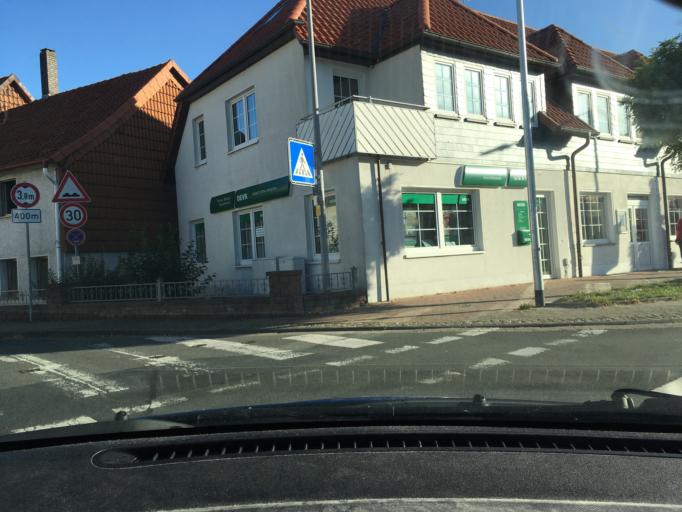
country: DE
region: Lower Saxony
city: Springe
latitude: 52.2082
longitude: 9.5494
